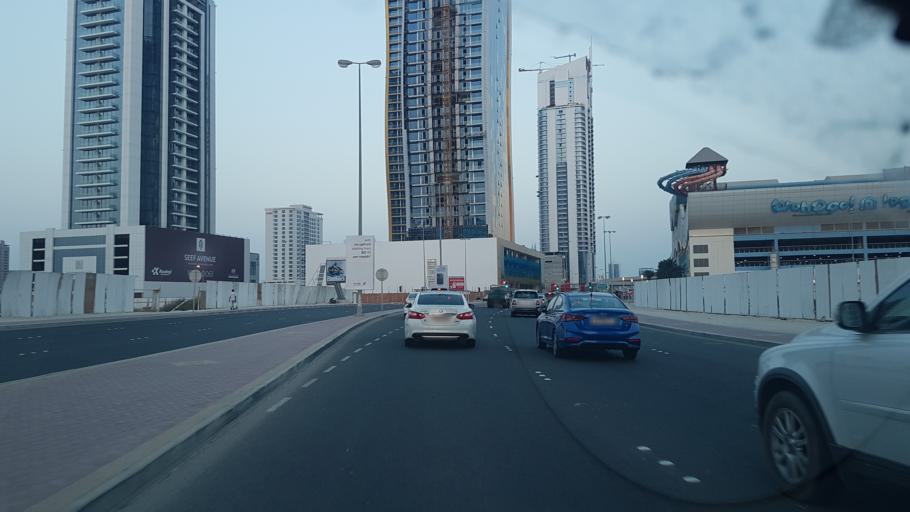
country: BH
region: Manama
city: Jidd Hafs
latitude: 26.2348
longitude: 50.5501
